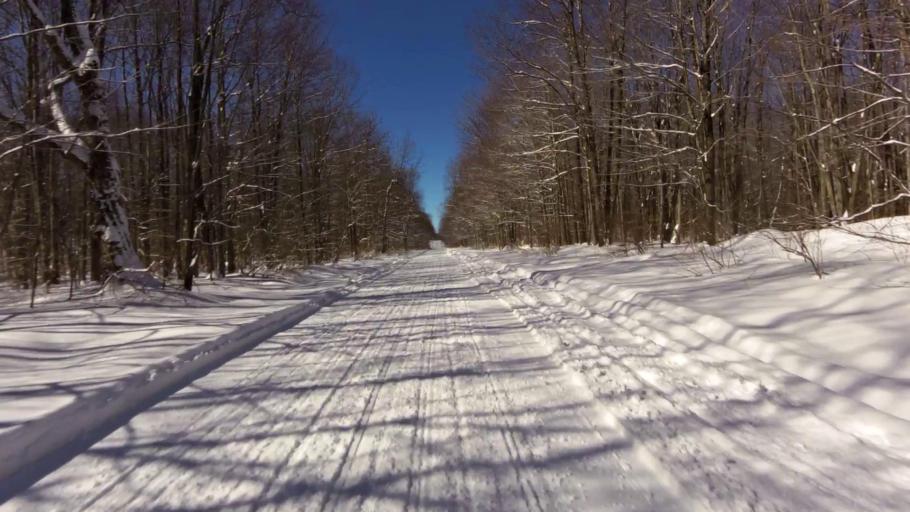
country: US
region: New York
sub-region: Chautauqua County
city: Mayville
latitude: 42.2334
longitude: -79.3716
